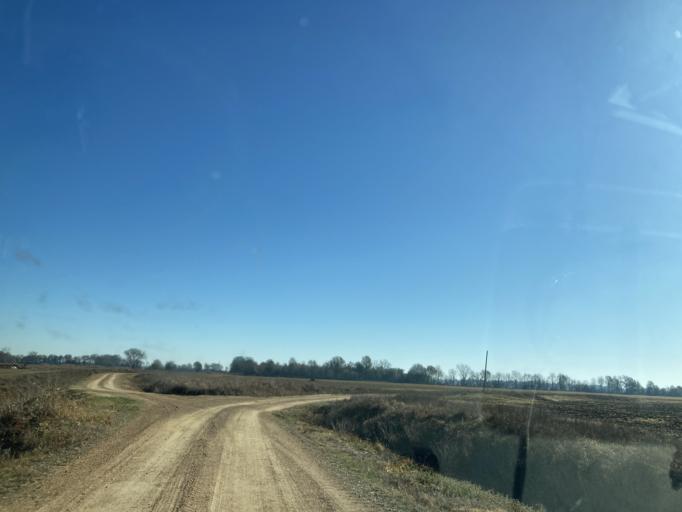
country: US
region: Mississippi
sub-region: Sharkey County
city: Rolling Fork
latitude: 32.9008
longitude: -90.6618
